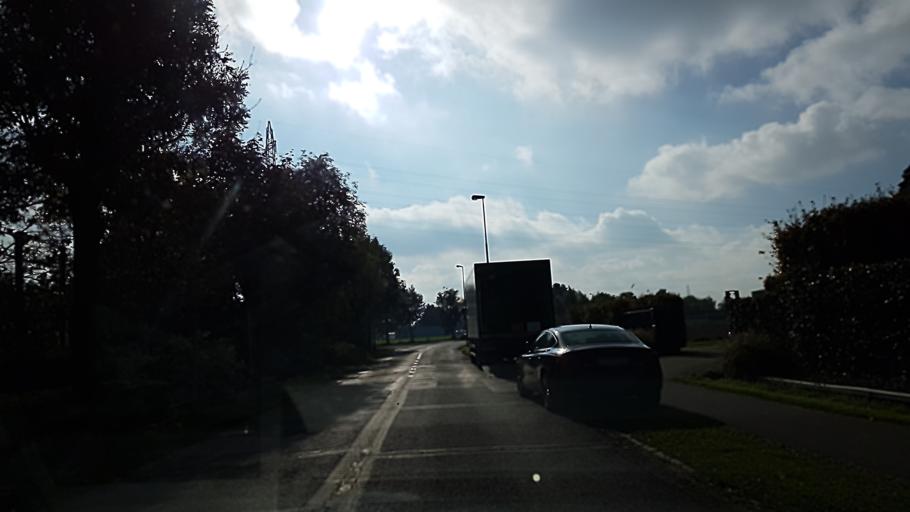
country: BE
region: Flanders
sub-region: Provincie Antwerpen
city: Aartselaar
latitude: 51.1204
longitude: 4.4070
